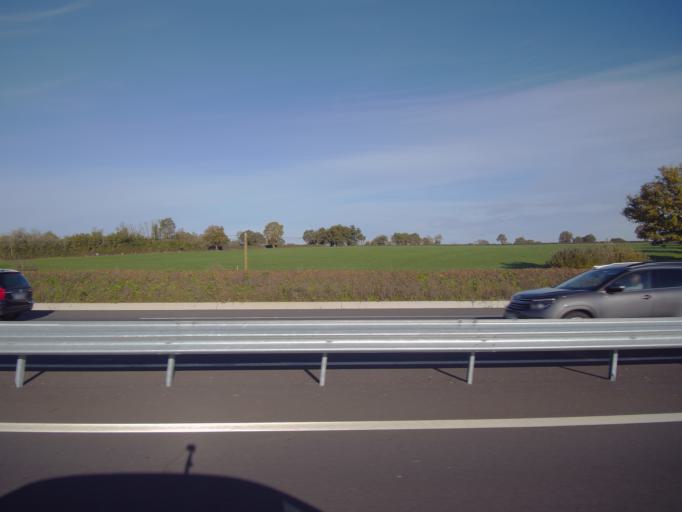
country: FR
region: Pays de la Loire
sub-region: Departement de Maine-et-Loire
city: Vihiers
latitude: 47.1348
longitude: -0.5879
